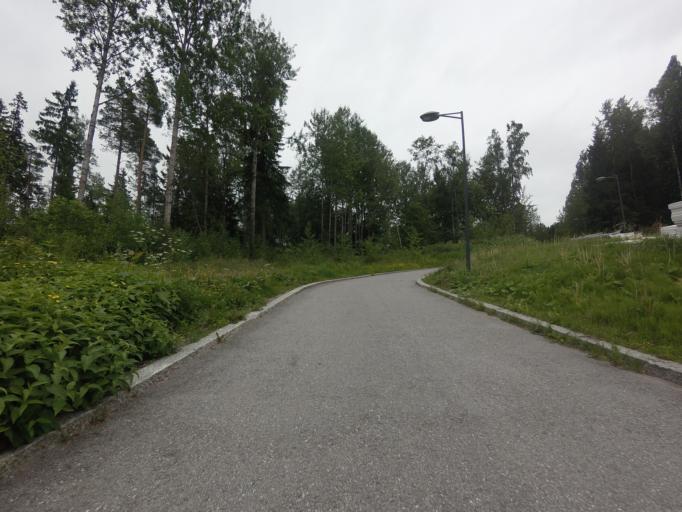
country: FI
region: Uusimaa
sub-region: Helsinki
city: Kauniainen
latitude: 60.1845
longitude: 24.7378
